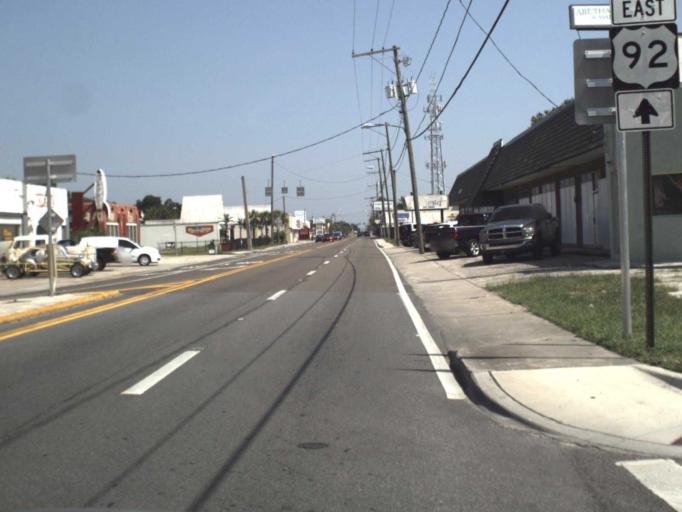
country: US
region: Florida
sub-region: Hillsborough County
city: Tampa
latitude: 27.9906
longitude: -82.4594
